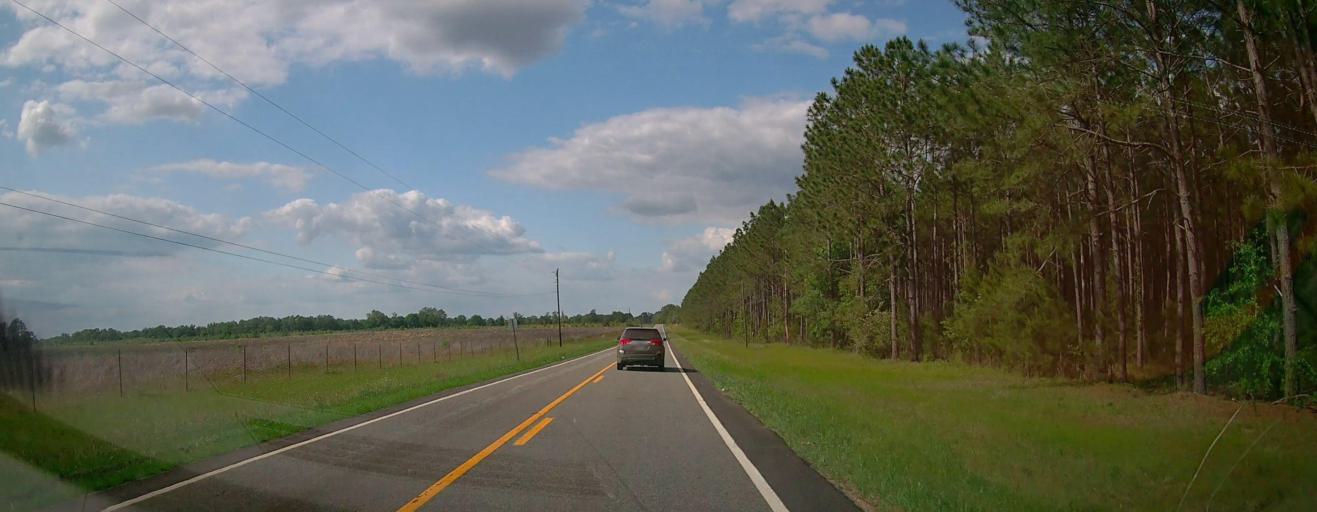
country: US
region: Georgia
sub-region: Laurens County
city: East Dublin
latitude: 32.6375
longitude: -82.8947
